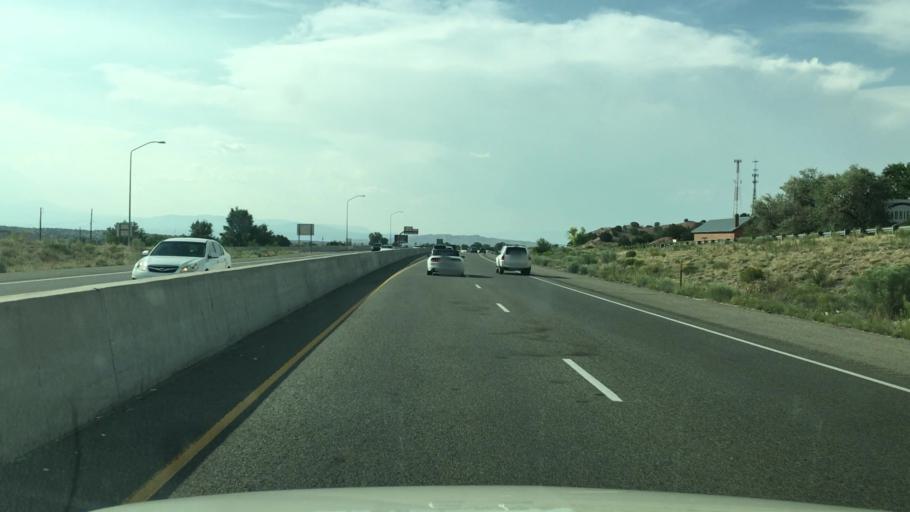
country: US
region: New Mexico
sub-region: Santa Fe County
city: Nambe
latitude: 35.8418
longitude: -105.9904
